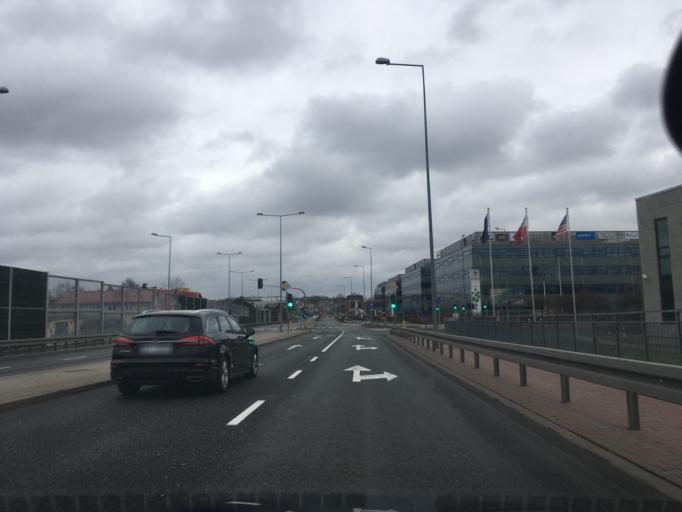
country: PL
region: Masovian Voivodeship
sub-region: Warszawa
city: Wlochy
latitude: 52.1564
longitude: 20.9936
